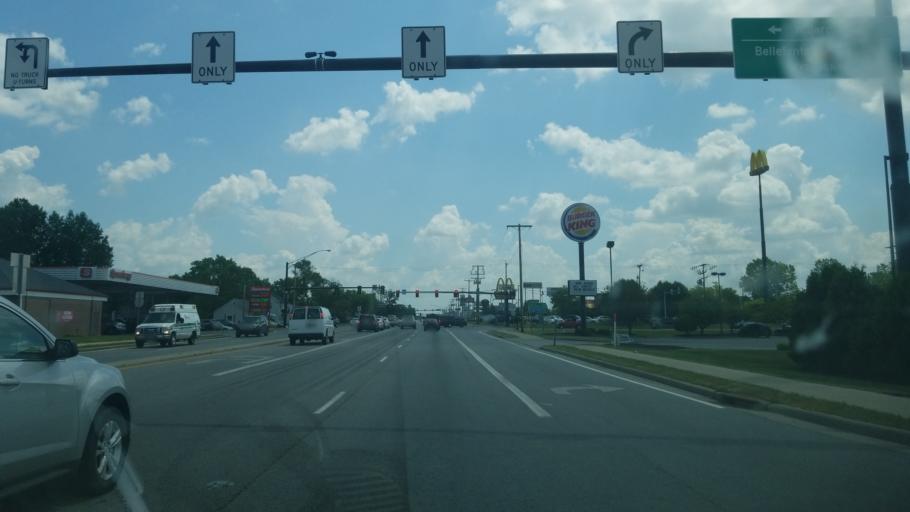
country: US
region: Ohio
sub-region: Allen County
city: Lima
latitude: 40.7306
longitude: -84.0723
